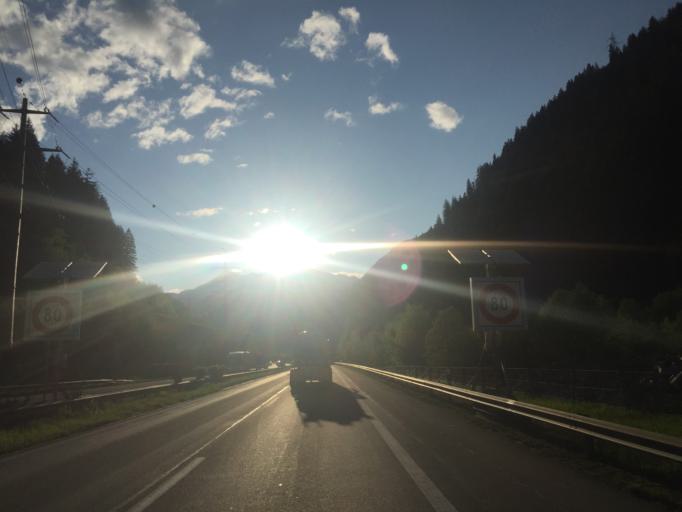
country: CH
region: Ticino
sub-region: Leventina District
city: Airolo
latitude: 46.5171
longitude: 8.6576
